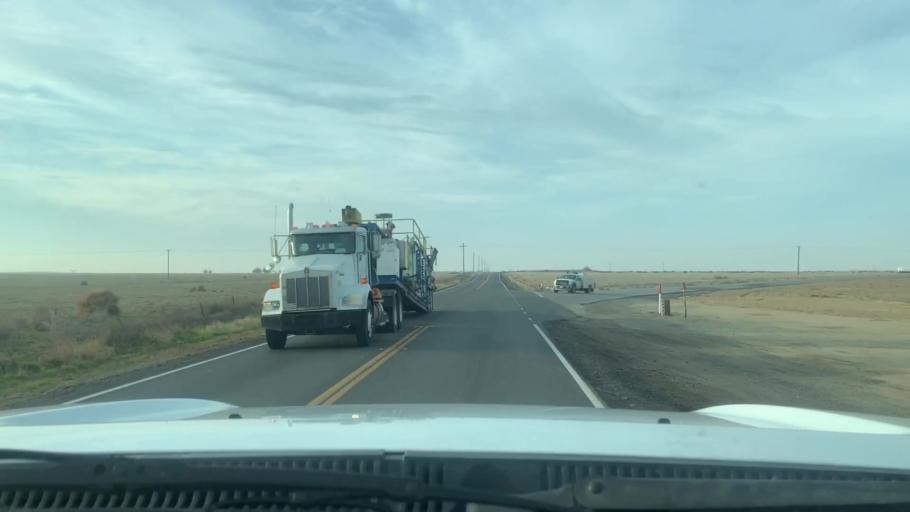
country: US
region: California
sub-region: Kern County
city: Lost Hills
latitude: 35.5575
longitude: -119.7971
